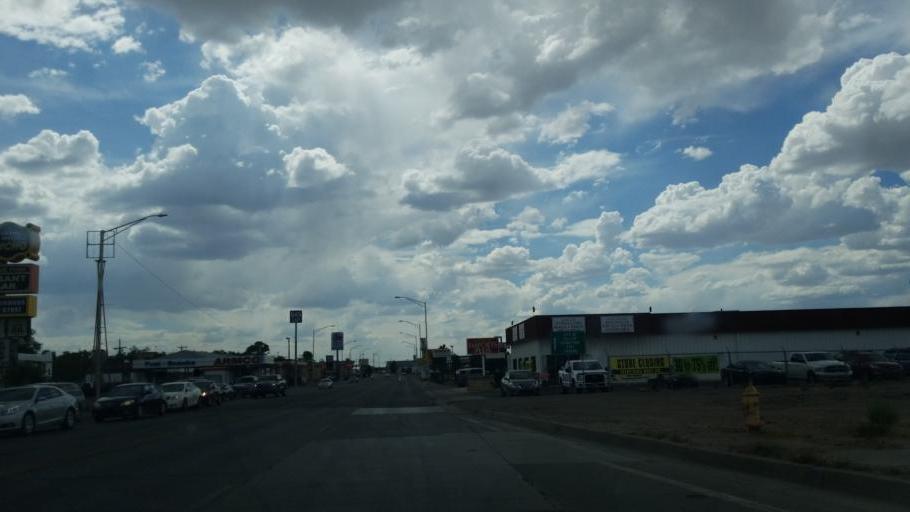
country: US
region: New Mexico
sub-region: McKinley County
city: Gallup
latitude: 35.5301
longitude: -108.7275
